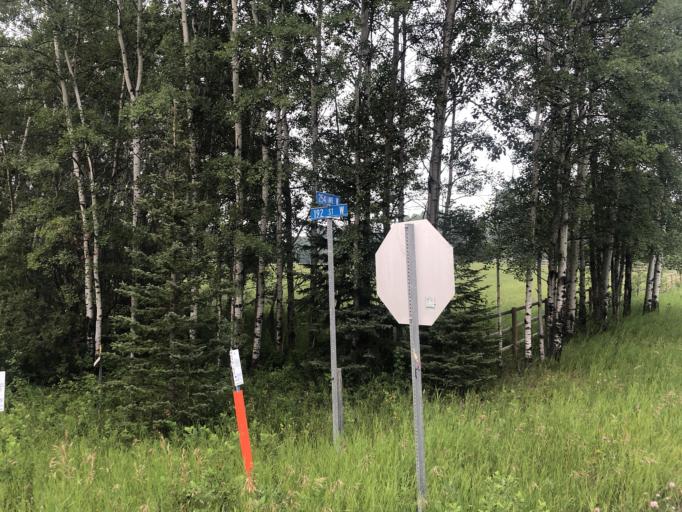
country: CA
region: Alberta
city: Black Diamond
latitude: 50.8237
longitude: -114.2788
